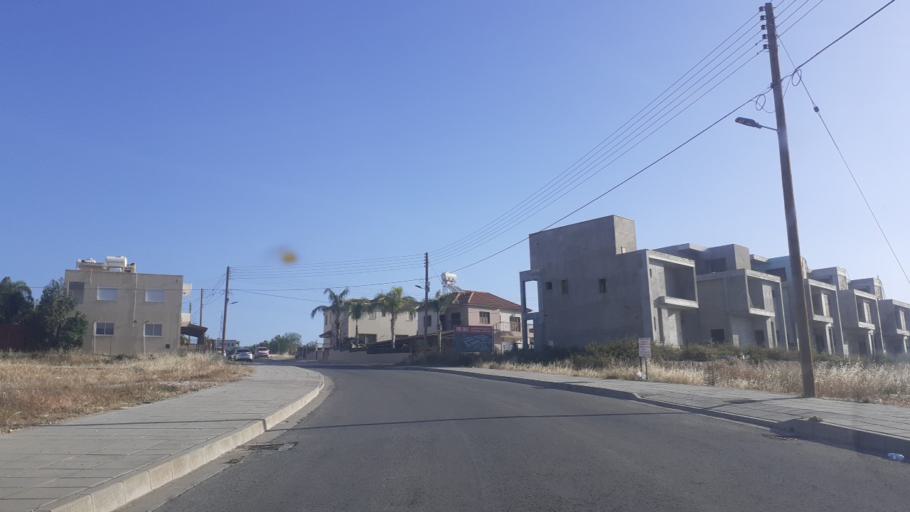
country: CY
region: Limassol
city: Ypsonas
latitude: 34.6986
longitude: 32.9417
